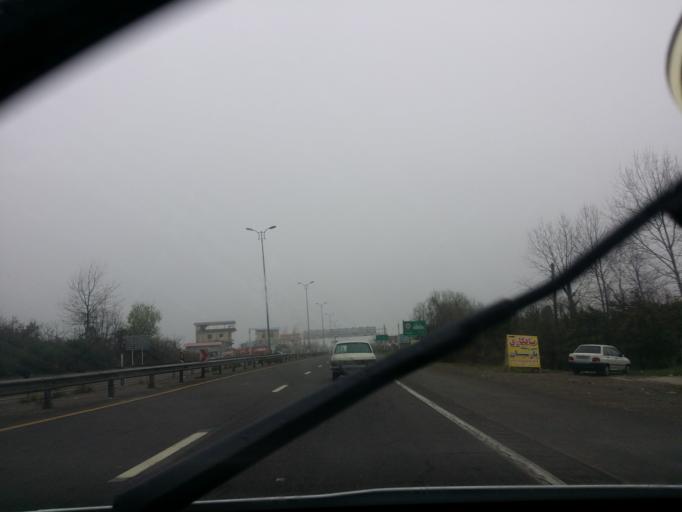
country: IR
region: Mazandaran
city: Tonekabon
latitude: 36.8212
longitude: 50.8473
